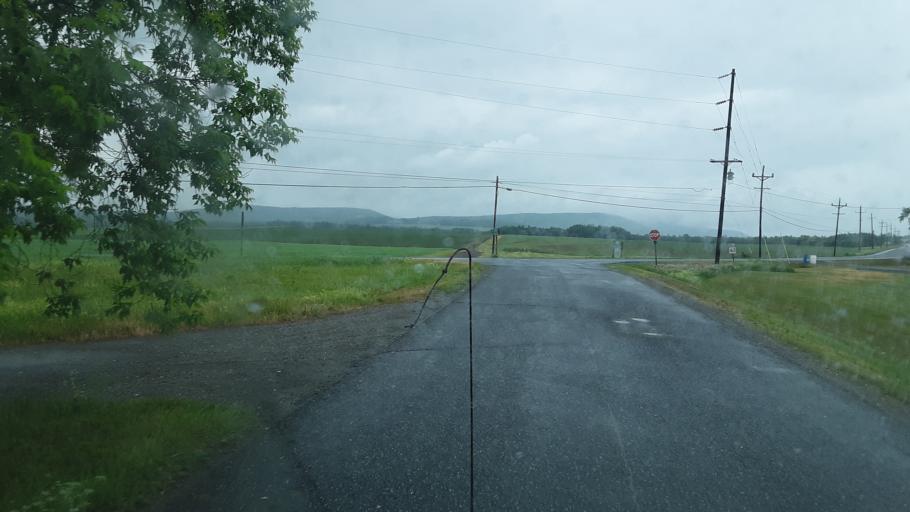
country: US
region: Maine
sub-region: Aroostook County
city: Presque Isle
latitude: 46.6815
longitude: -68.1733
